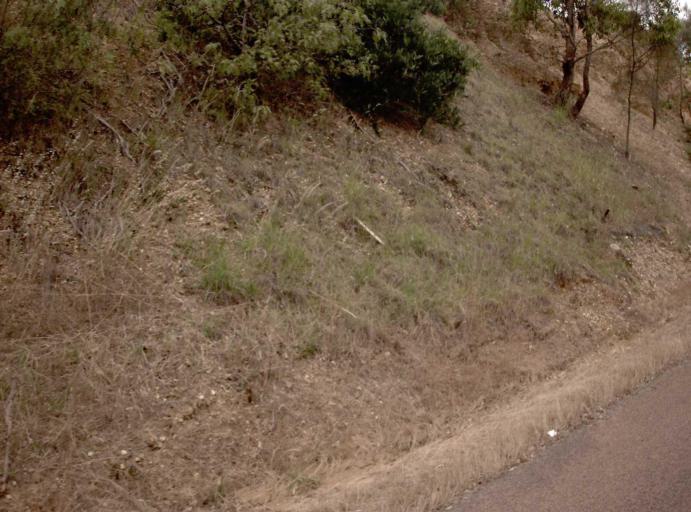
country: AU
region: Victoria
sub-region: East Gippsland
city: Bairnsdale
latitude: -37.8920
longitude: 147.6588
